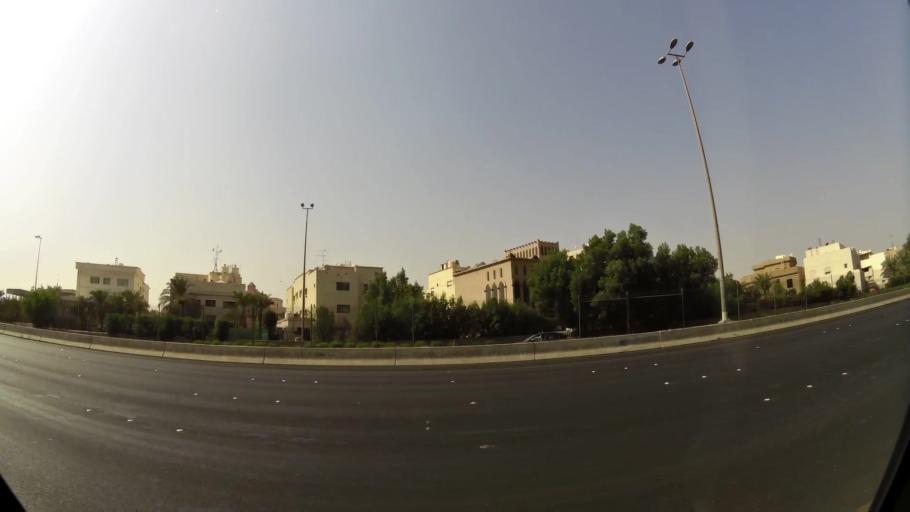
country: KW
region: Muhafazat Hawalli
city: Hawalli
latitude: 29.3333
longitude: 48.0058
